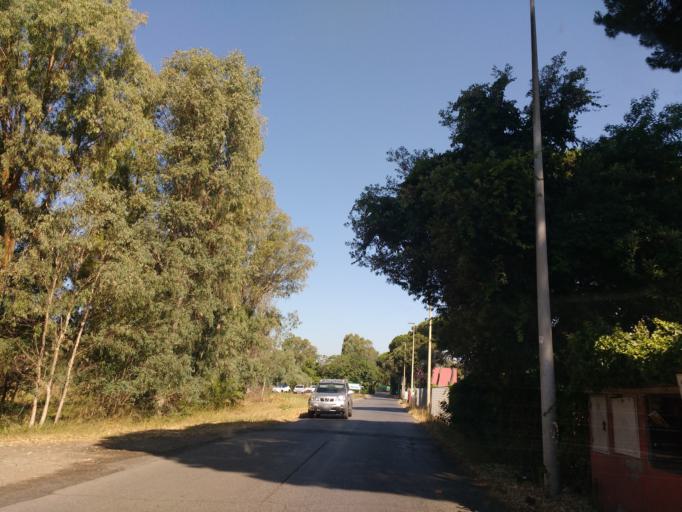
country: IT
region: Latium
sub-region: Citta metropolitana di Roma Capitale
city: Acilia-Castel Fusano-Ostia Antica
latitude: 41.7452
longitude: 12.3192
